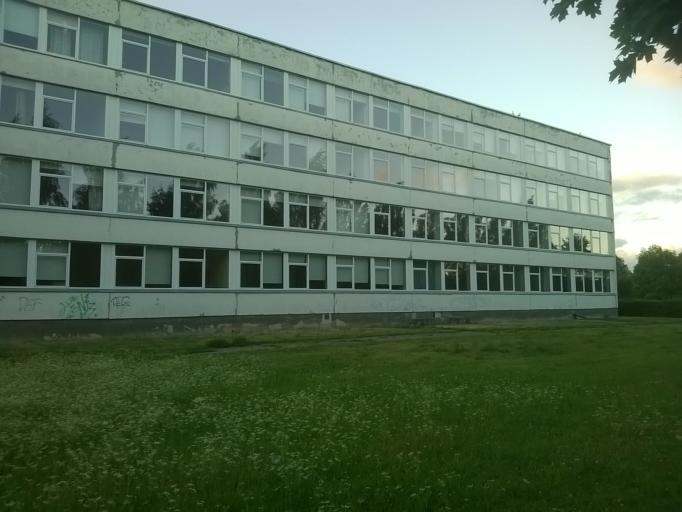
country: EE
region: Tartu
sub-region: Tartu linn
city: Tartu
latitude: 58.3506
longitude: 26.7147
